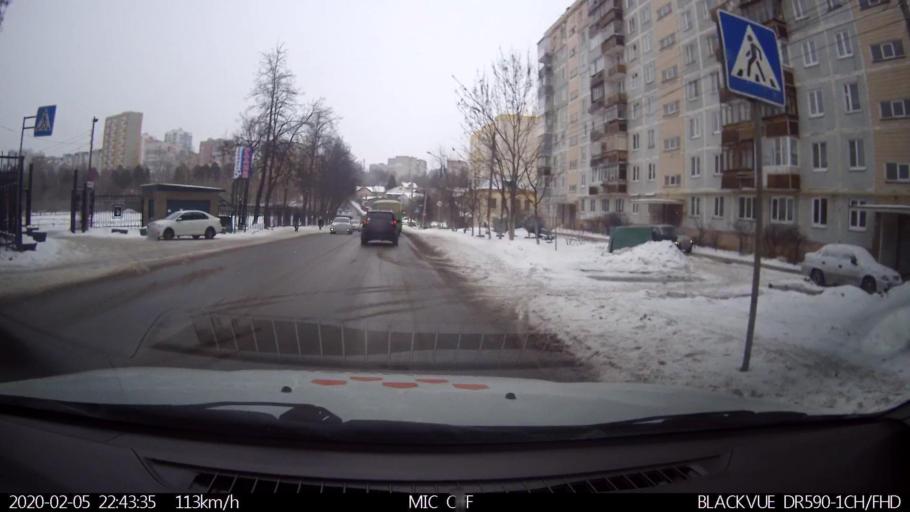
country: RU
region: Nizjnij Novgorod
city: Imeni Stepana Razina
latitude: 54.7119
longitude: 44.3812
